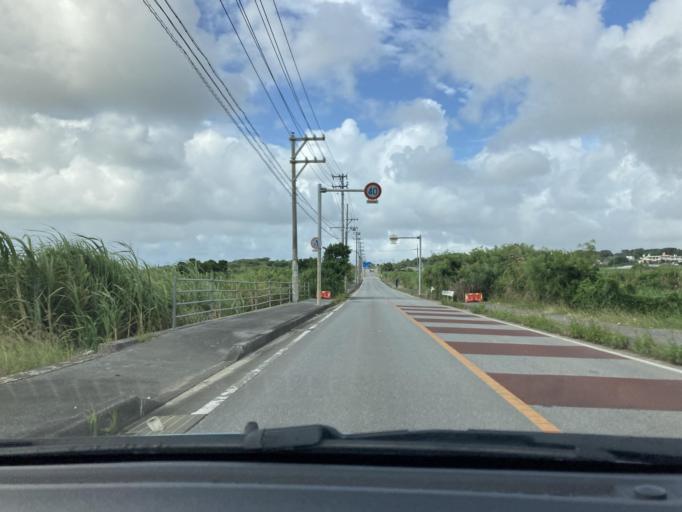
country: JP
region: Okinawa
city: Itoman
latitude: 26.1122
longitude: 127.6923
